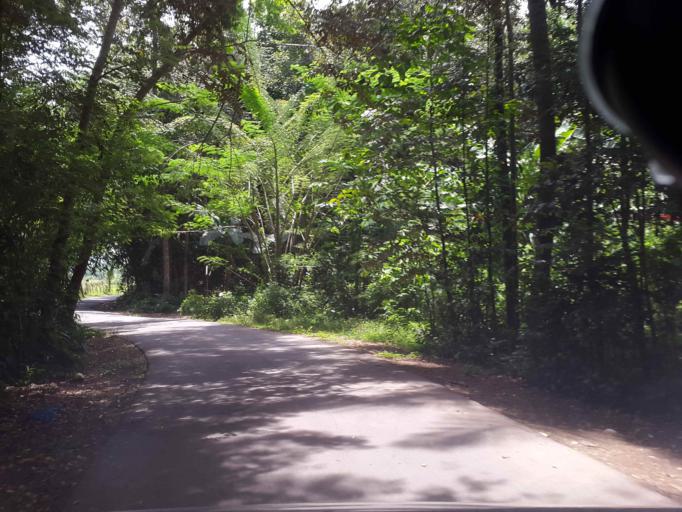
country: ID
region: West Nusa Tenggara
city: Karangkebon Timur
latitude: -8.6781
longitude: 116.0972
